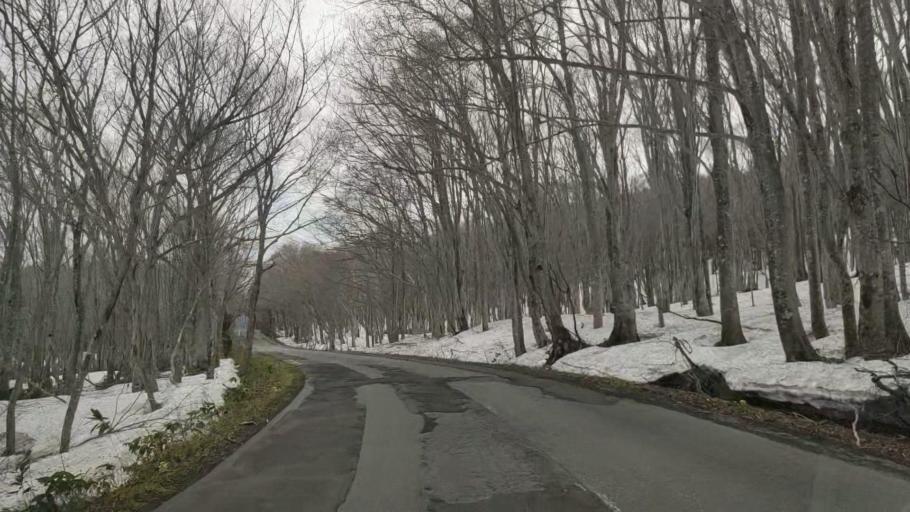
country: JP
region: Aomori
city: Aomori Shi
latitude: 40.6982
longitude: 140.9033
